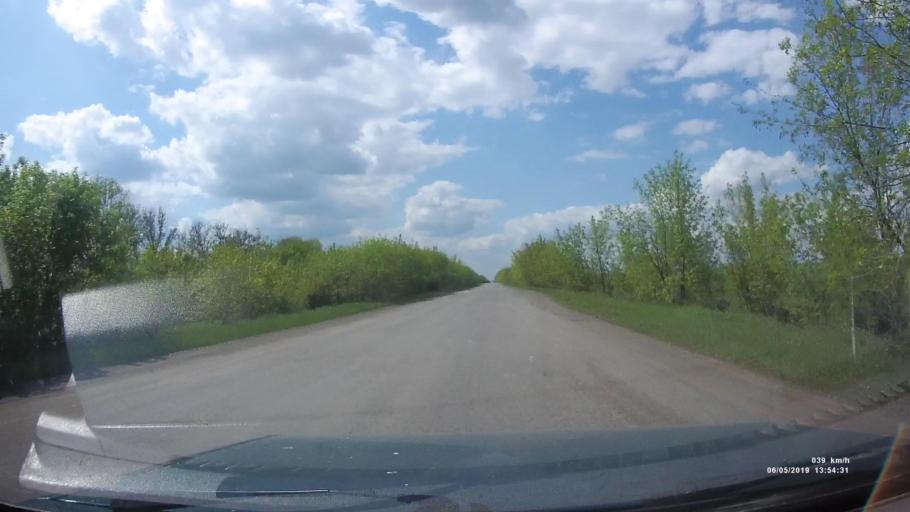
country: RU
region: Rostov
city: Melikhovskaya
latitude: 47.6743
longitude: 40.4478
